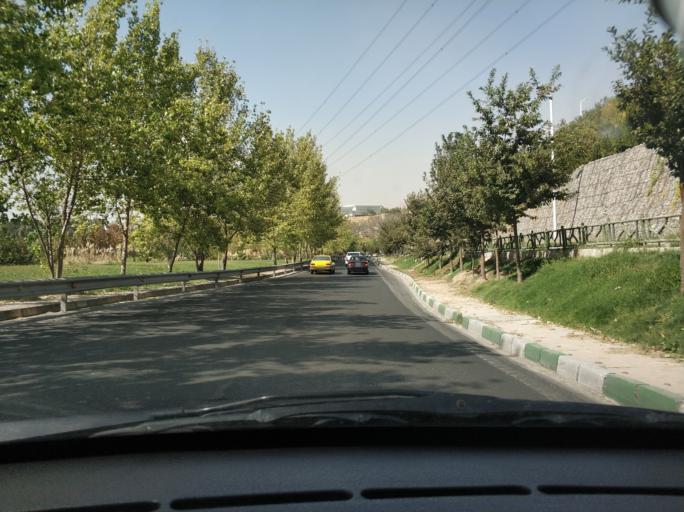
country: IR
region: Tehran
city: Tehran
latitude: 35.7412
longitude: 51.3726
